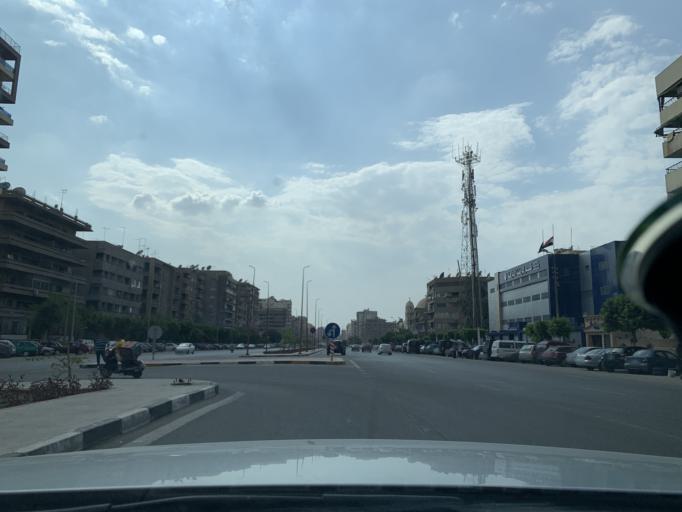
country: EG
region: Muhafazat al Qahirah
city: Cairo
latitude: 30.1066
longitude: 31.3415
